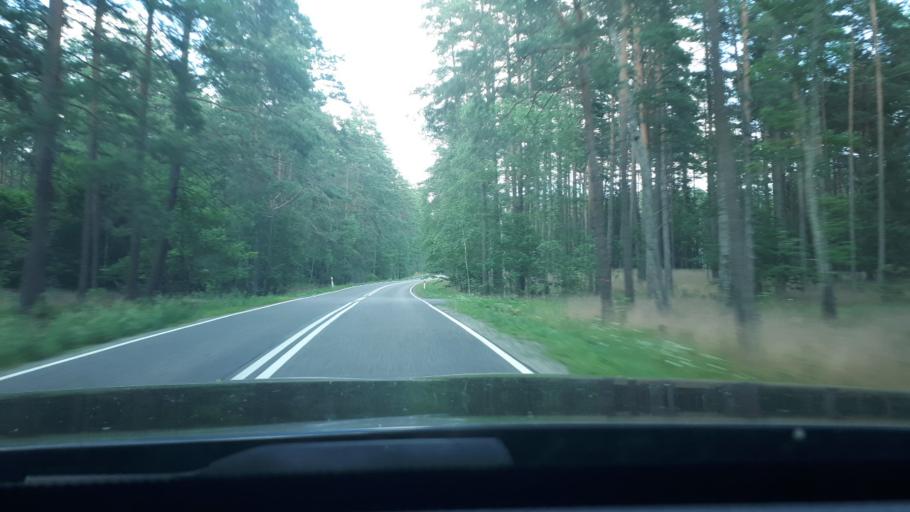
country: PL
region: Warmian-Masurian Voivodeship
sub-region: Powiat olsztynski
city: Stawiguda
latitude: 53.5373
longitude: 20.5216
